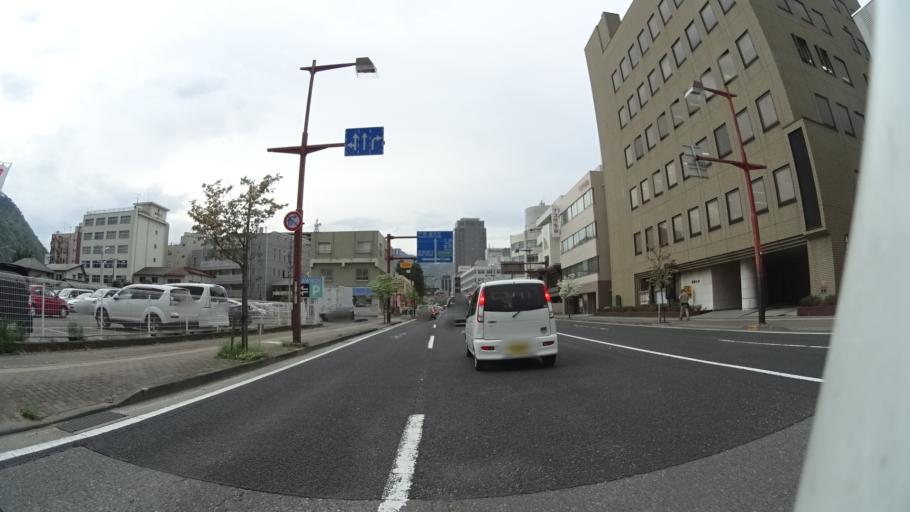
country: JP
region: Nagano
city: Nagano-shi
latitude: 36.6489
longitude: 138.1820
